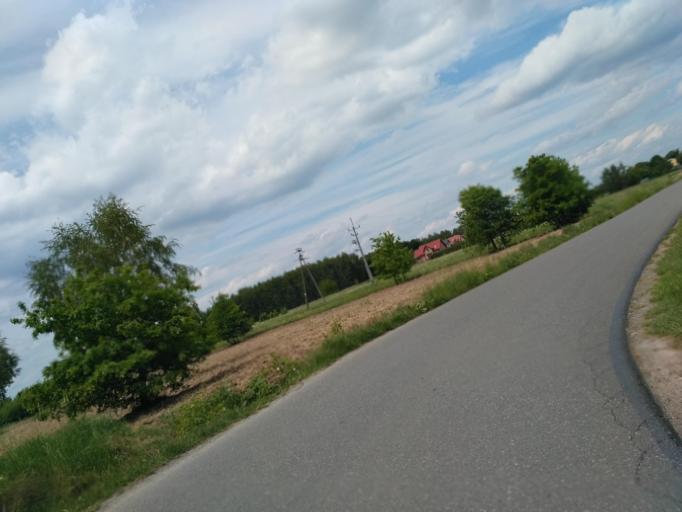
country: PL
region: Subcarpathian Voivodeship
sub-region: Powiat krosnienski
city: Chorkowka
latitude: 49.6827
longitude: 21.7035
